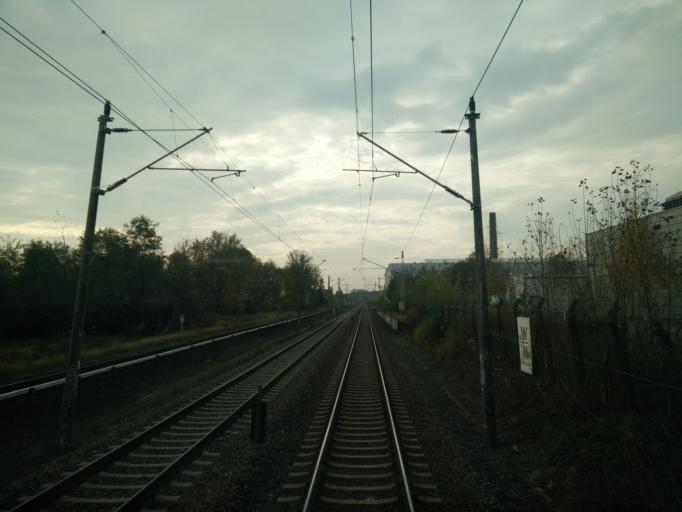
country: DE
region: Brandenburg
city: Wildau
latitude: 52.3260
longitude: 13.6363
